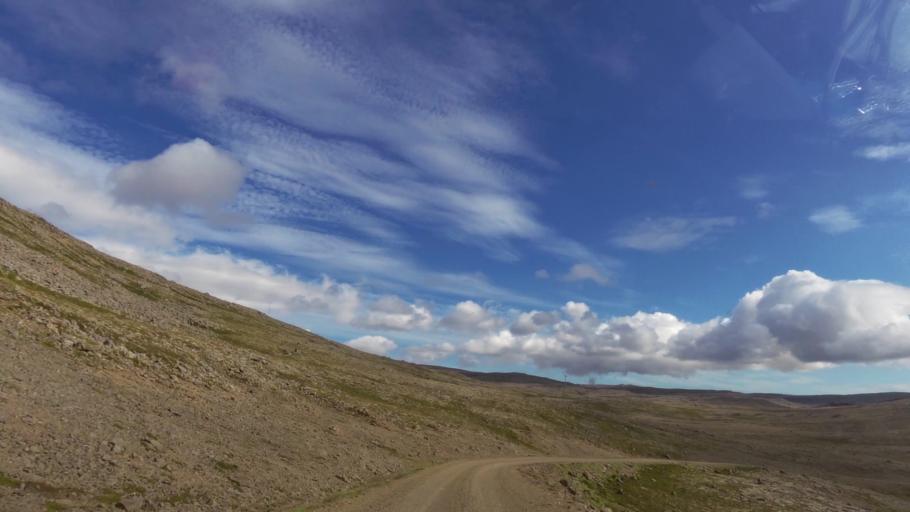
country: IS
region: West
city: Olafsvik
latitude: 65.6163
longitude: -24.3052
